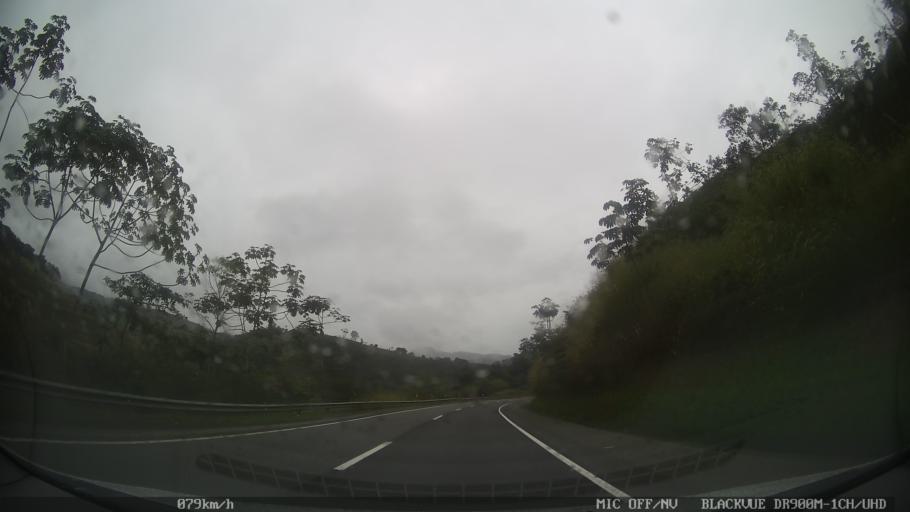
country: BR
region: Sao Paulo
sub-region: Cajati
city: Cajati
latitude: -24.8102
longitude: -48.2120
